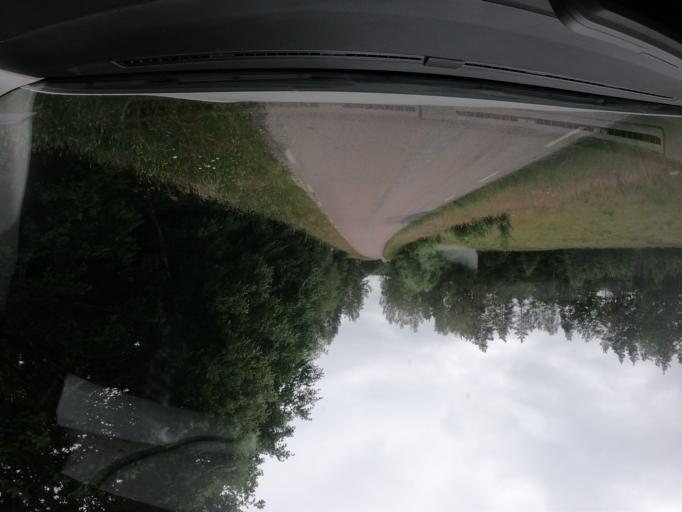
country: SE
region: Skane
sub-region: Perstorps Kommun
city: Perstorp
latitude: 56.1083
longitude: 13.3512
